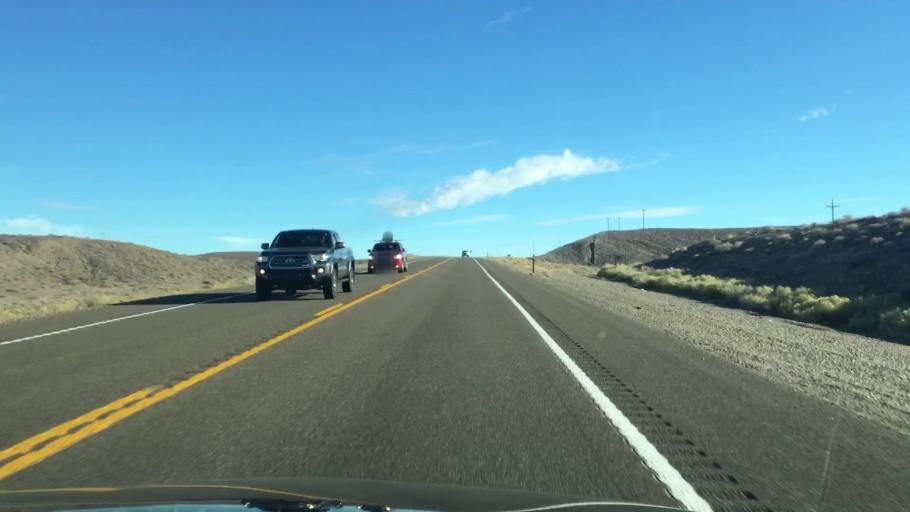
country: US
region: Nevada
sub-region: Mineral County
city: Hawthorne
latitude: 38.2208
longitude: -118.0089
